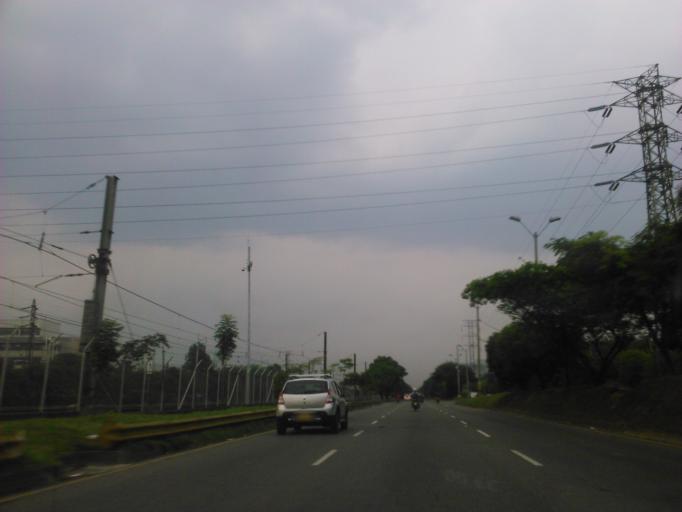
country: CO
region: Antioquia
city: Itagui
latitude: 6.2075
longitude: -75.5786
